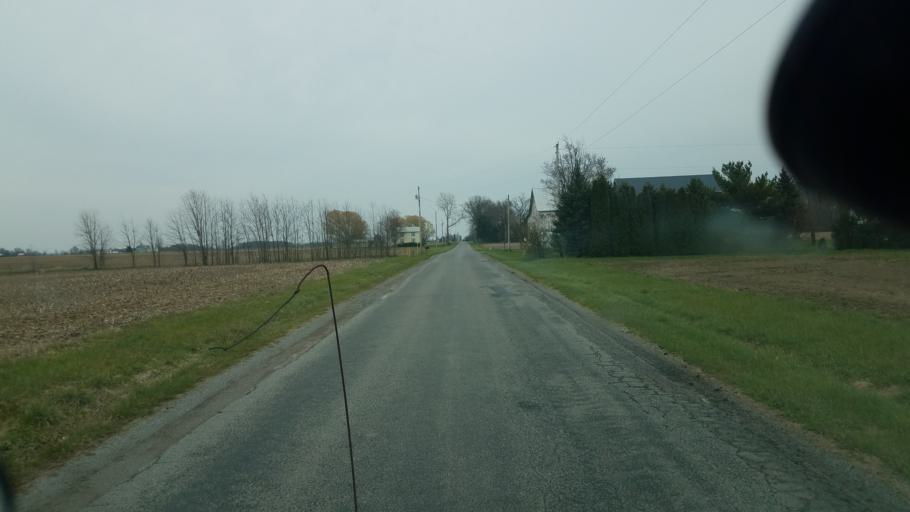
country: US
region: Ohio
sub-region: Hardin County
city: Forest
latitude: 40.8908
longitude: -83.5258
